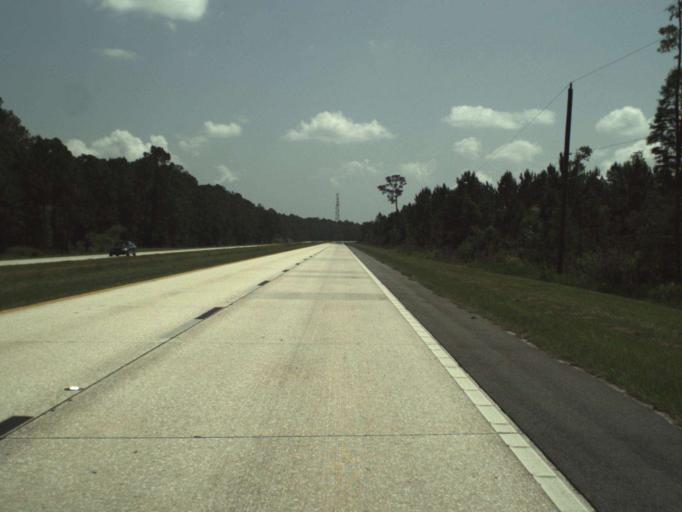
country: US
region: Florida
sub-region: Volusia County
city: Samsula-Spruce Creek
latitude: 29.1282
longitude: -81.1613
